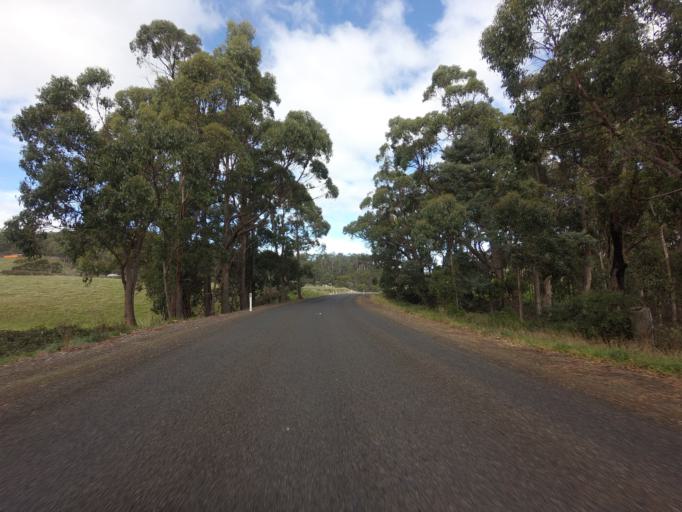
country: AU
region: Tasmania
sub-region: Clarence
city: Sandford
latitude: -43.0747
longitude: 147.7497
